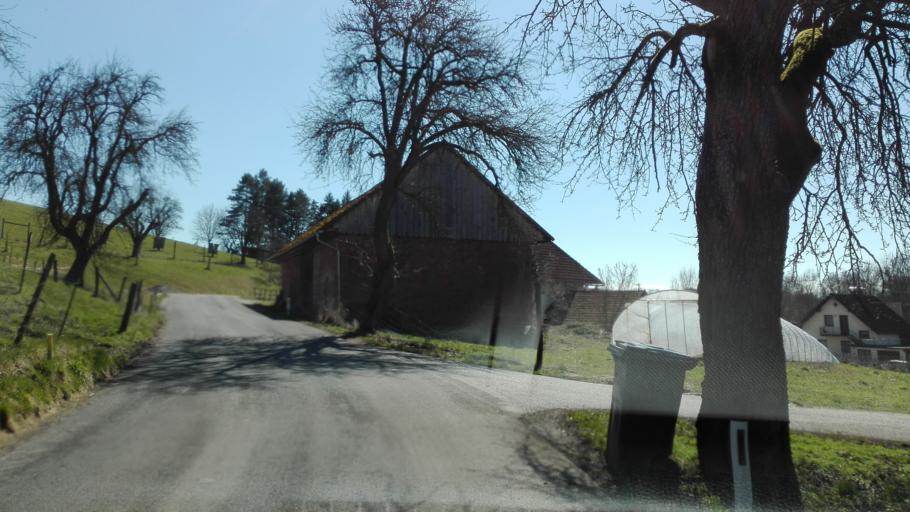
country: AT
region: Upper Austria
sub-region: Wels-Land
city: Buchkirchen
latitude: 48.2312
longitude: 13.9725
